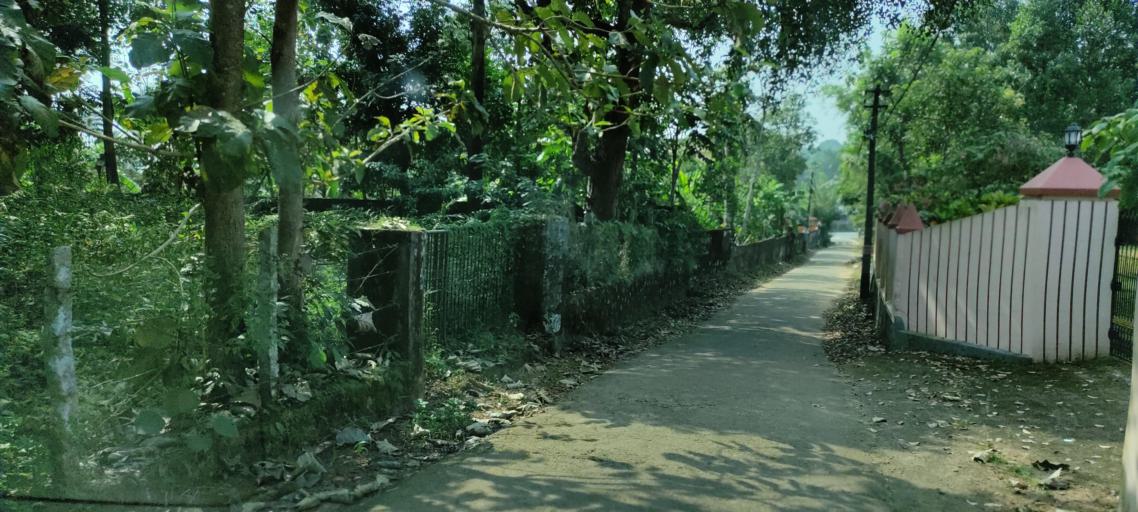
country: IN
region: Kerala
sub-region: Pattanamtitta
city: Adur
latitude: 9.2102
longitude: 76.6881
